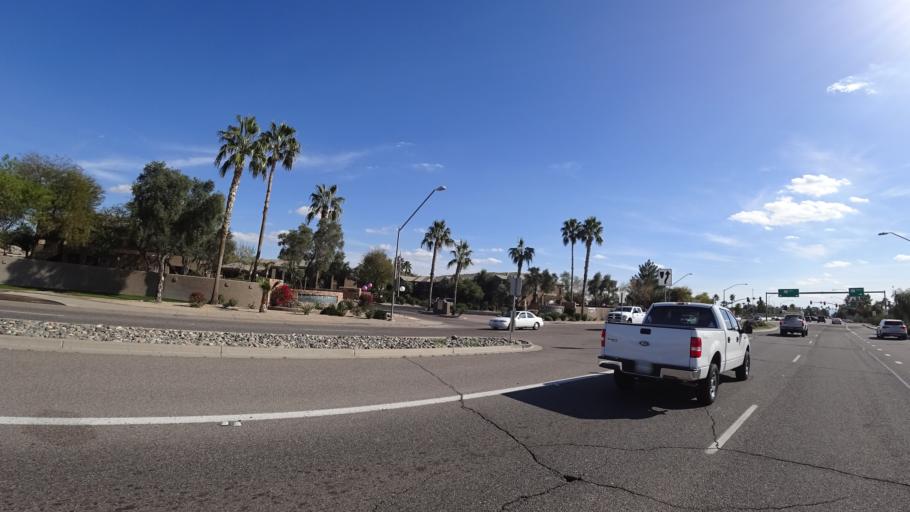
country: US
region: Arizona
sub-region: Maricopa County
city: Sun City
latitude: 33.6698
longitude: -112.2205
